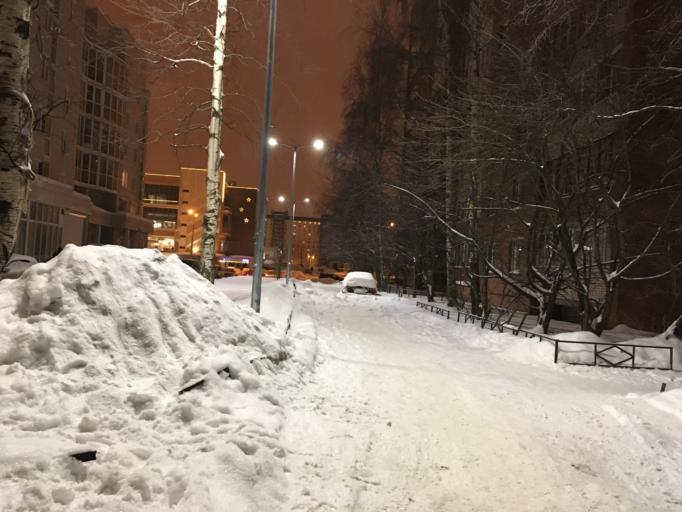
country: RU
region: St.-Petersburg
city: Staraya Derevnya
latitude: 60.0097
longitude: 30.2456
